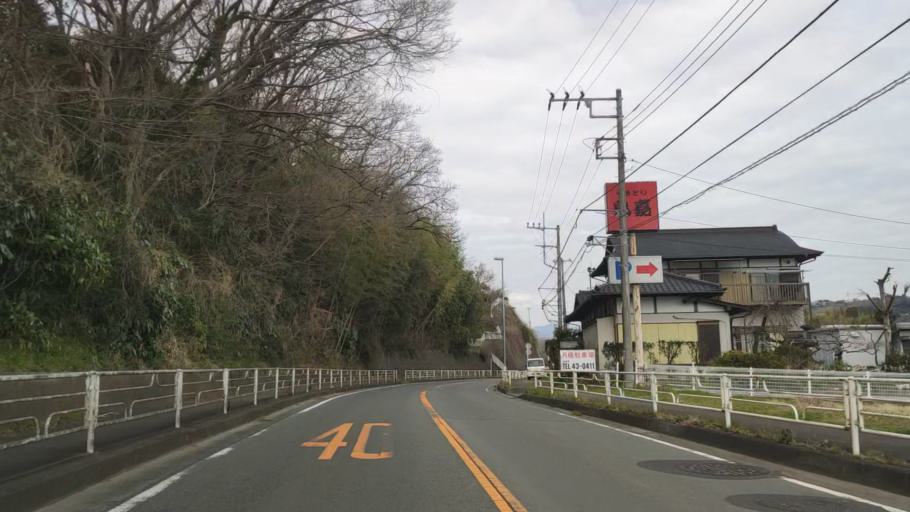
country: JP
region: Kanagawa
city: Ninomiya
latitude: 35.3065
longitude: 139.2262
